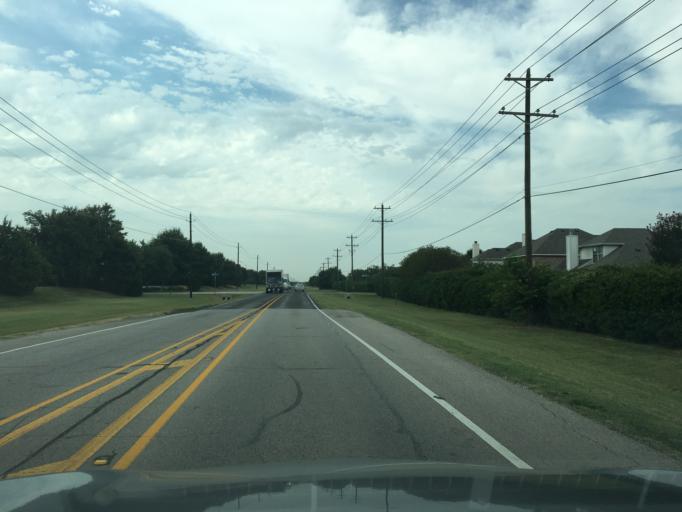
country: US
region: Texas
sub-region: Collin County
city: Parker
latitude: 33.0835
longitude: -96.6202
